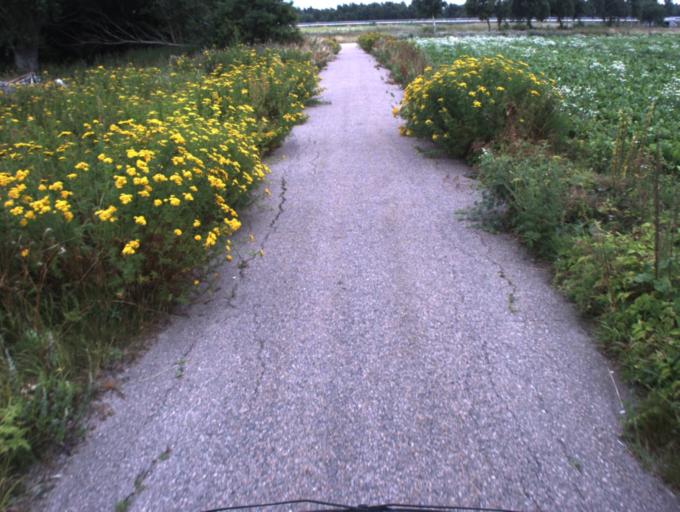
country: SE
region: Skane
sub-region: Helsingborg
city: Odakra
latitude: 56.0890
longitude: 12.7597
